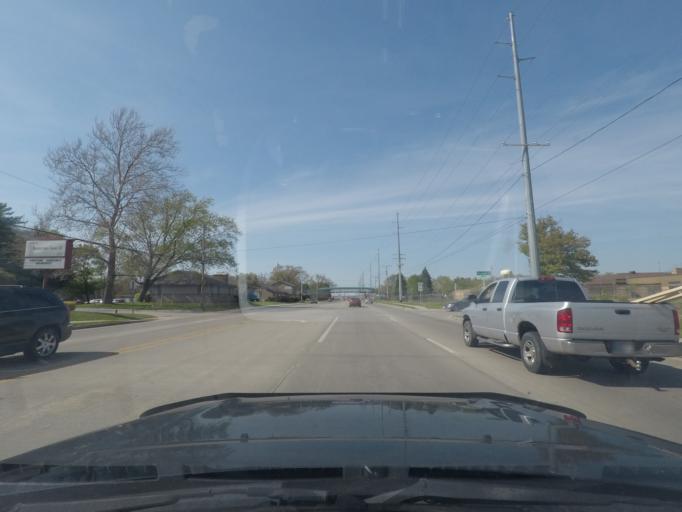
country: US
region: Indiana
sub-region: Elkhart County
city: Elkhart
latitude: 41.6836
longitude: -86.0034
